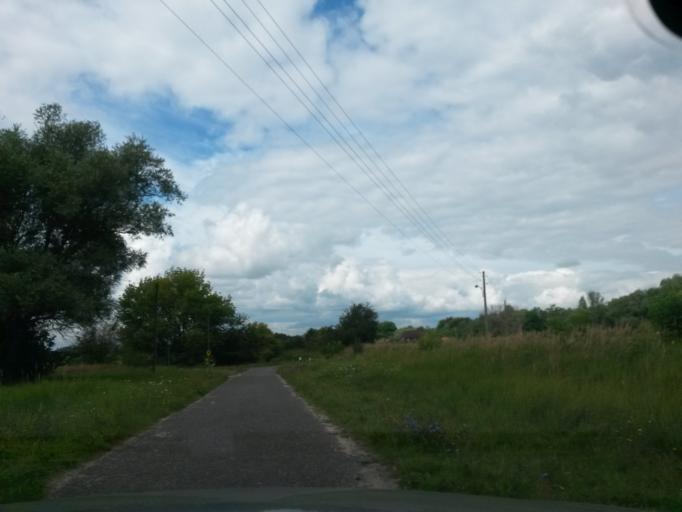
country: PL
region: West Pomeranian Voivodeship
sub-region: Powiat gryfinski
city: Cedynia
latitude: 52.8653
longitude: 14.1394
